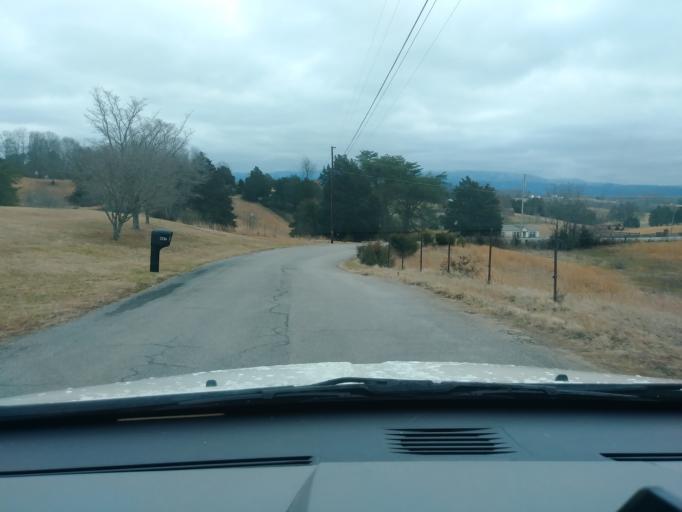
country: US
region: Tennessee
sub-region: Greene County
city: Greeneville
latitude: 36.0999
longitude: -82.8834
